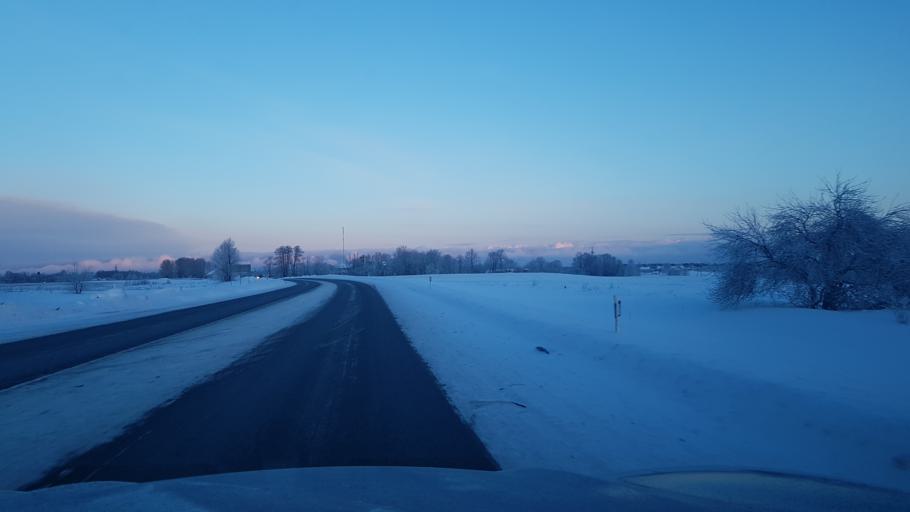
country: EE
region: Ida-Virumaa
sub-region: Narva-Joesuu linn
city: Narva-Joesuu
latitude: 59.3957
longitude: 28.0788
